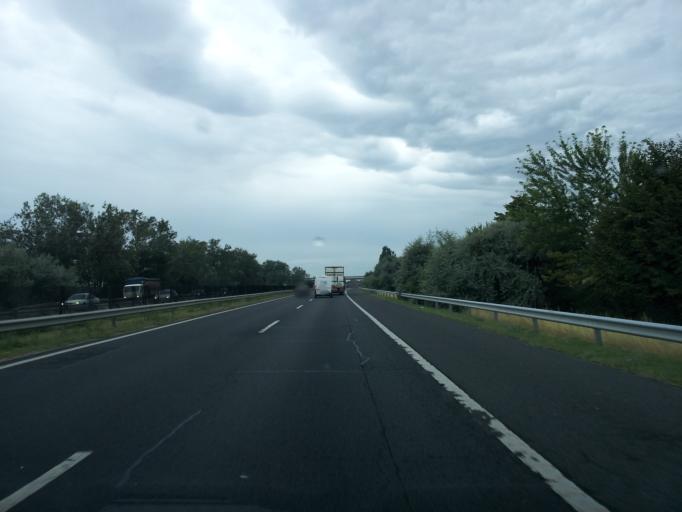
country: HU
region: Fejer
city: Kapolnasnyek
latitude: 47.2771
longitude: 18.7060
